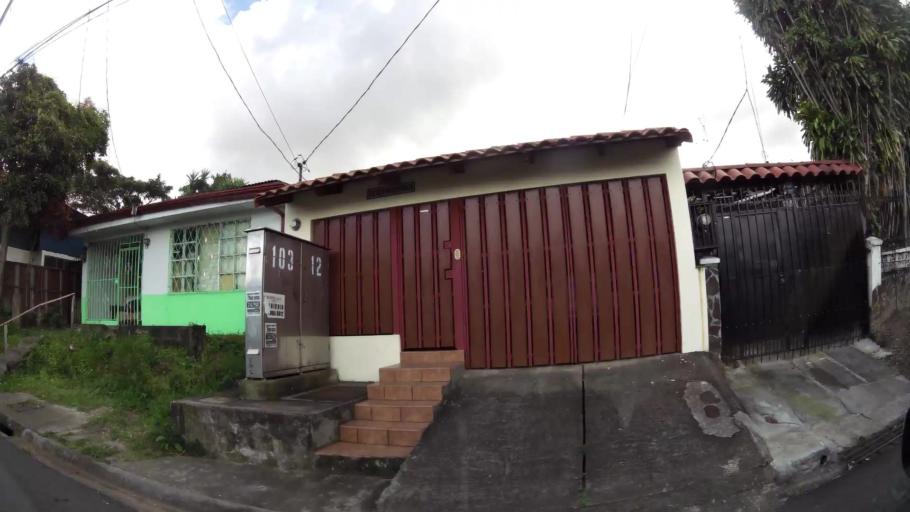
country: CR
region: San Jose
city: Escazu
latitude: 9.9151
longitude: -84.1404
